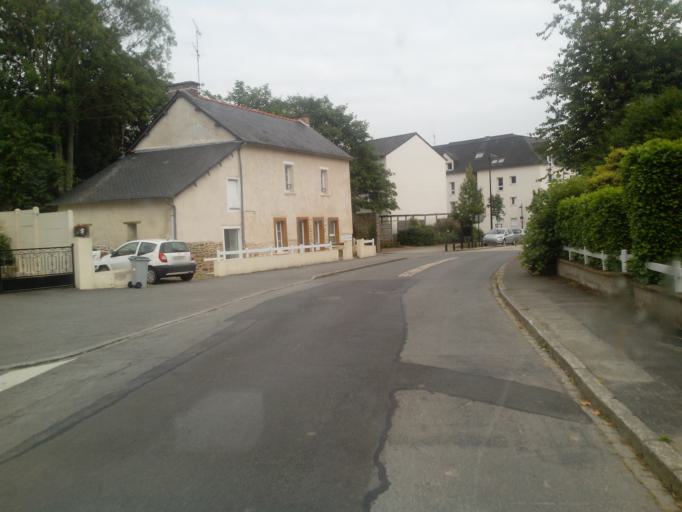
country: FR
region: Brittany
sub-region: Departement d'Ille-et-Vilaine
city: Acigne
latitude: 48.1329
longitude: -1.5380
